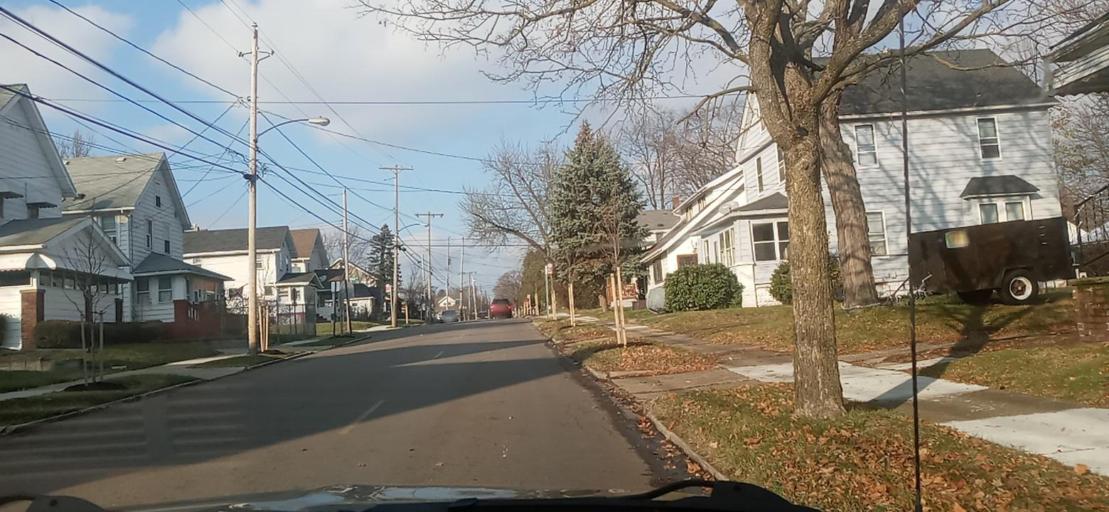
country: US
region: Ohio
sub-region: Summit County
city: Portage Lakes
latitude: 41.0477
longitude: -81.5575
